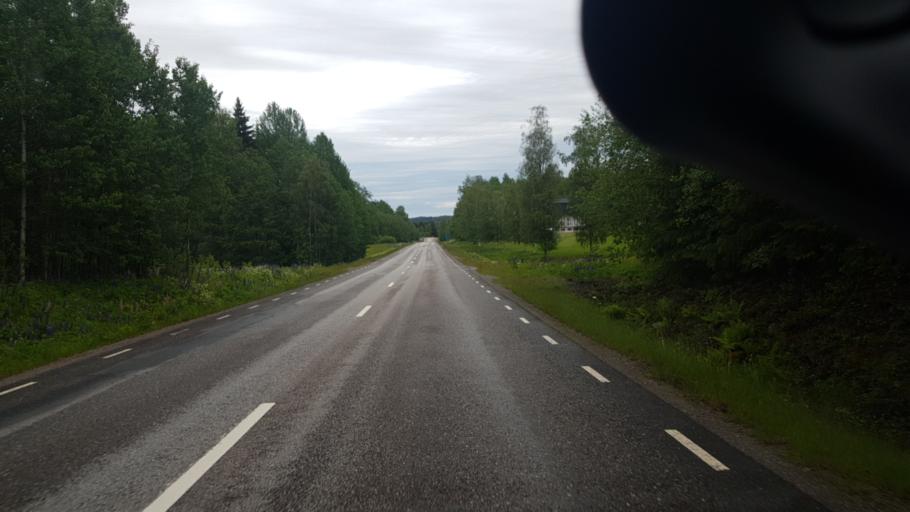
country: SE
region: Vaermland
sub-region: Eda Kommun
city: Amotfors
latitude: 59.7231
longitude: 12.1733
